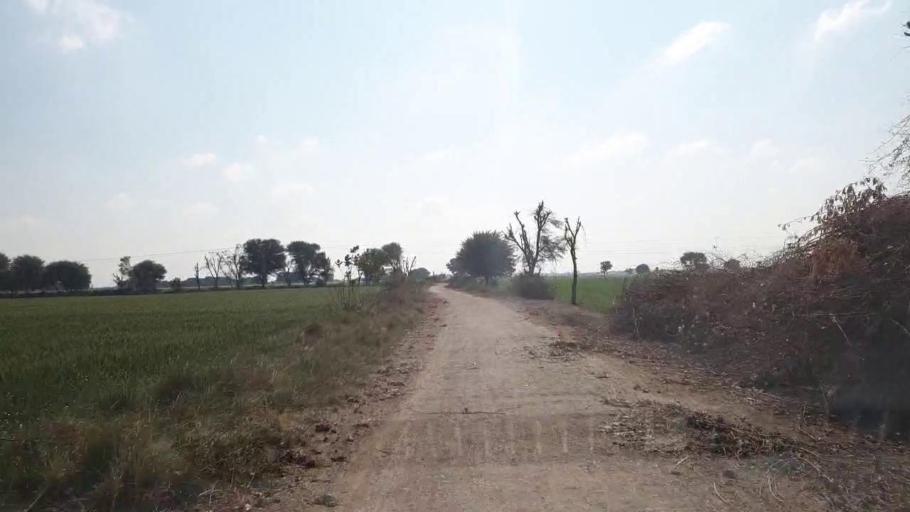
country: PK
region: Sindh
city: Shahpur Chakar
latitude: 26.0528
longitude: 68.5993
